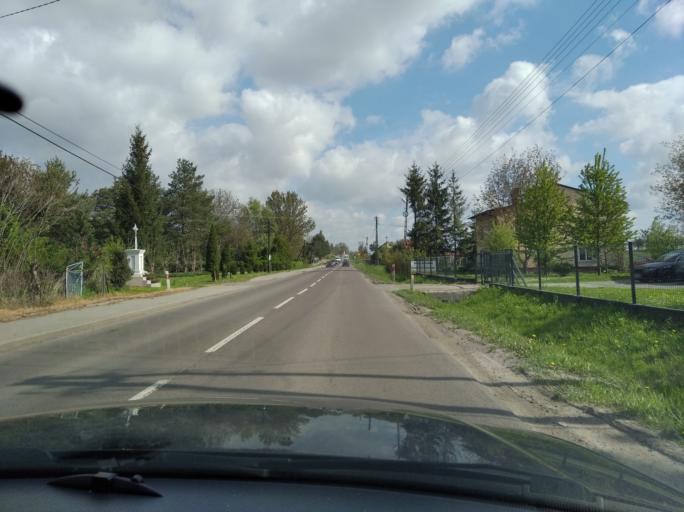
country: PL
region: Subcarpathian Voivodeship
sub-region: Powiat przeworski
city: Urzejowice
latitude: 50.0168
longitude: 22.4620
